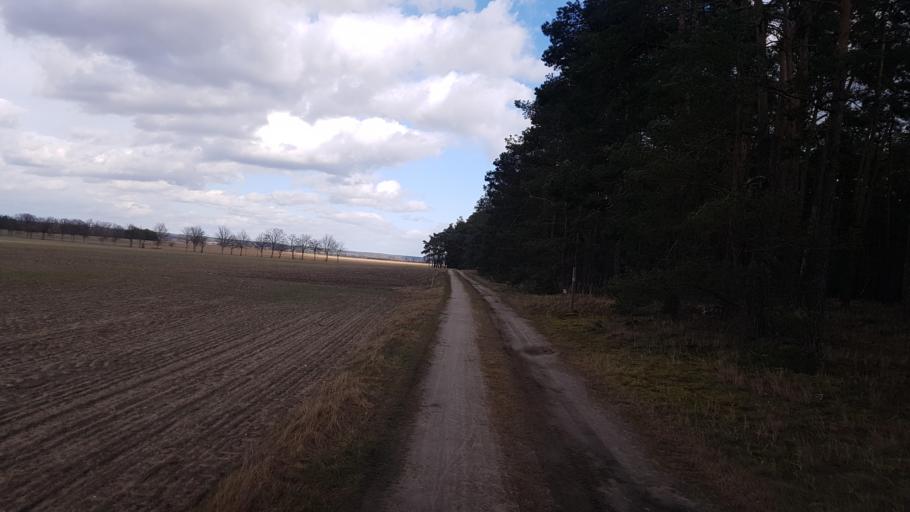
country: DE
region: Brandenburg
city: Schlieben
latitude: 51.6932
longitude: 13.4092
